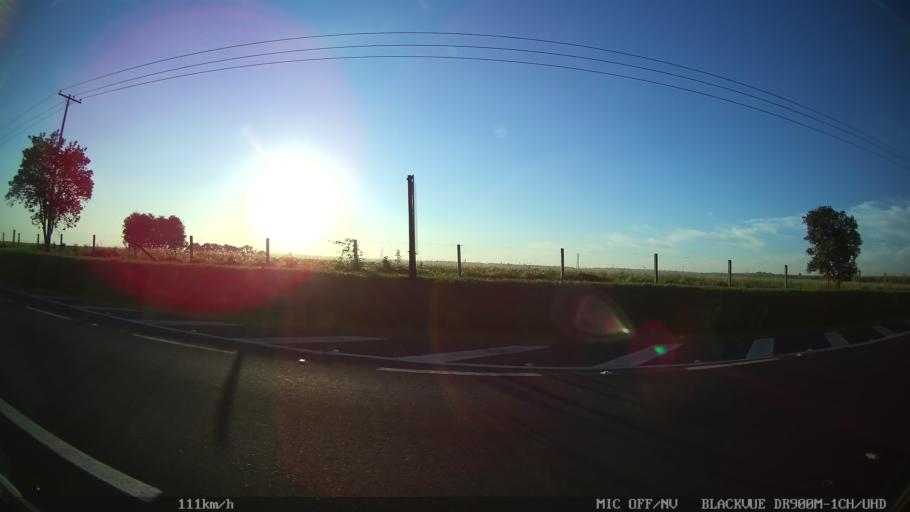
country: BR
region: Sao Paulo
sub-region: Araraquara
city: Araraquara
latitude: -21.8151
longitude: -48.2047
